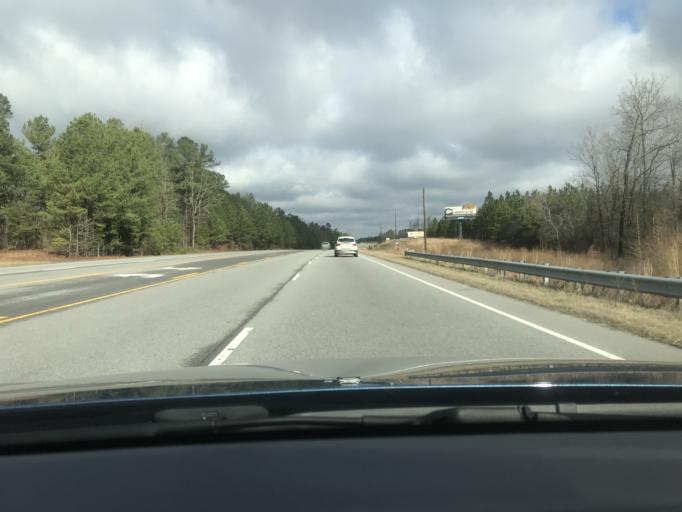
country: US
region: North Carolina
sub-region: Lee County
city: Broadway
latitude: 35.3529
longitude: -79.1091
